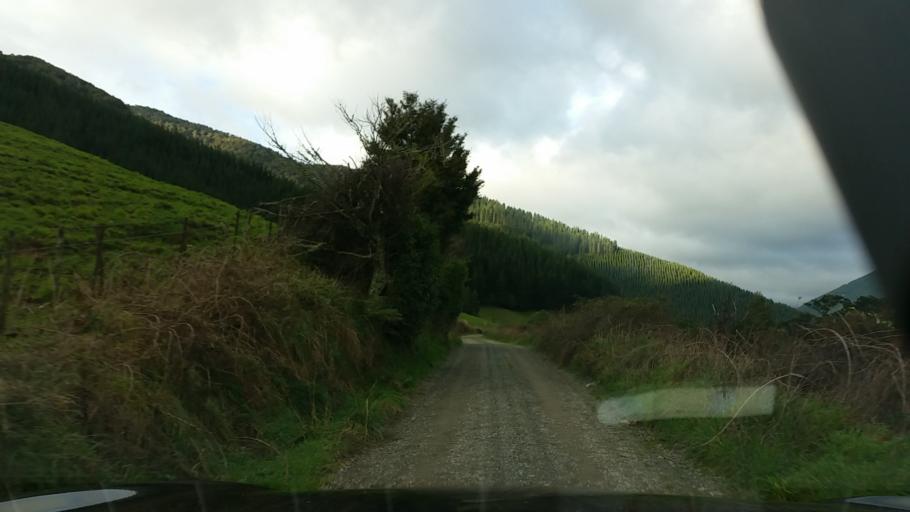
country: NZ
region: Nelson
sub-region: Nelson City
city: Nelson
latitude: -41.2084
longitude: 173.6360
